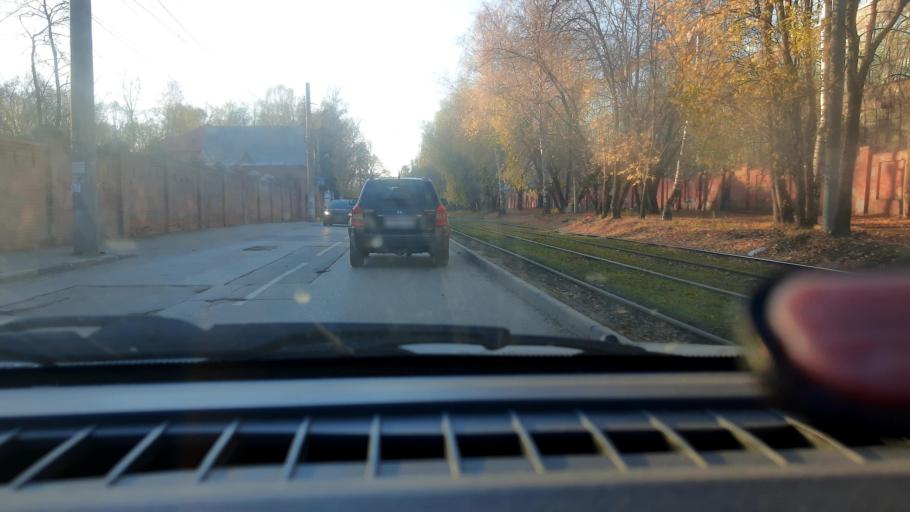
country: RU
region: Nizjnij Novgorod
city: Nizhniy Novgorod
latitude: 56.3004
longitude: 43.9916
